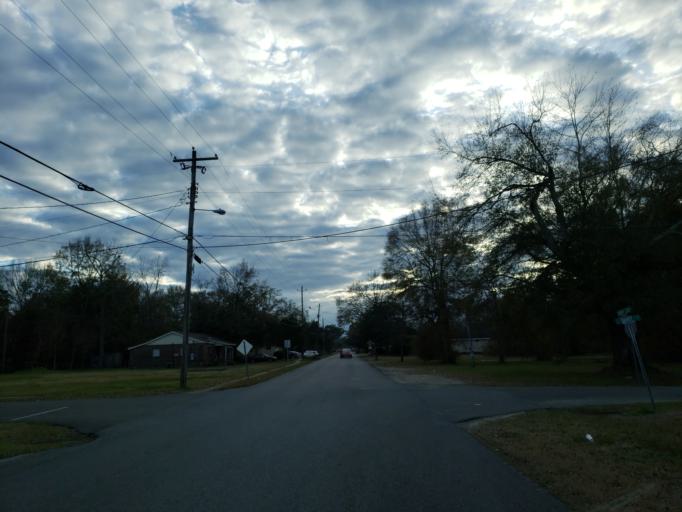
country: US
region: Mississippi
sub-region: Forrest County
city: Hattiesburg
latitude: 31.3095
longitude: -89.3053
